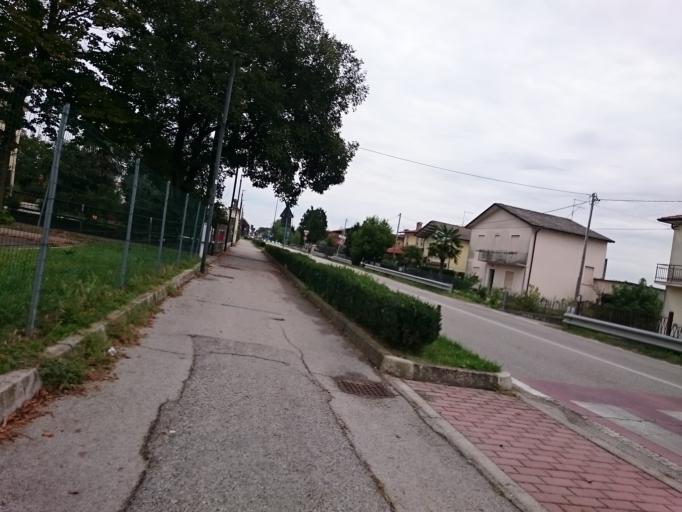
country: IT
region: Veneto
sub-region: Provincia di Vicenza
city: Quinto Vicentino
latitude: 45.5737
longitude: 11.6314
